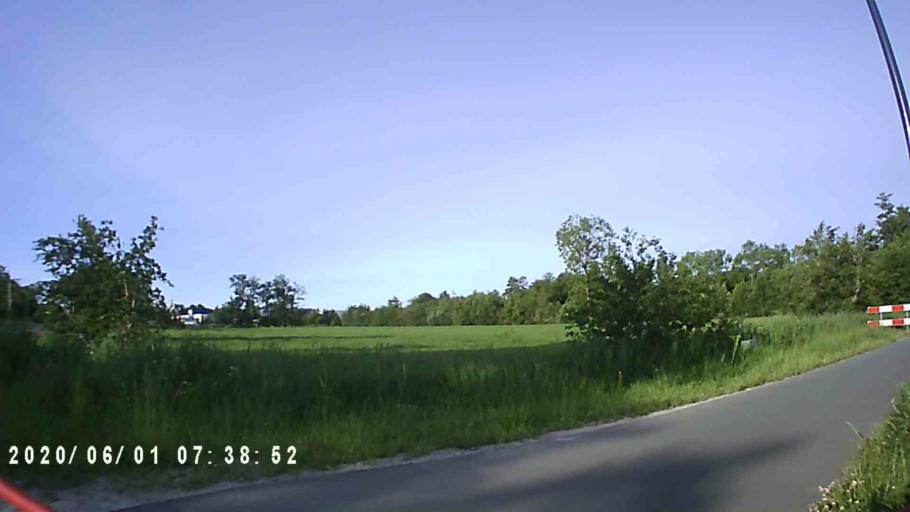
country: NL
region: Friesland
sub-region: Gemeente Dantumadiel
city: Damwald
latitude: 53.2964
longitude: 5.9964
